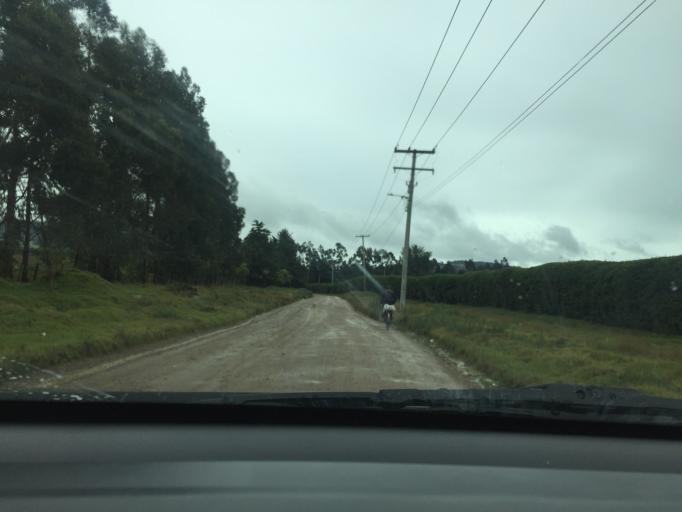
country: CO
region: Cundinamarca
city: El Rosal
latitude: 4.8359
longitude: -74.2892
